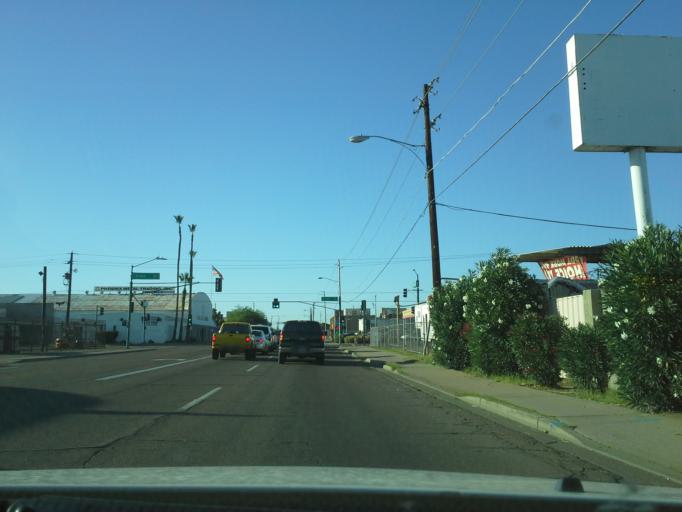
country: US
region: Arizona
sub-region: Maricopa County
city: Phoenix
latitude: 33.4405
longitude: -112.1000
